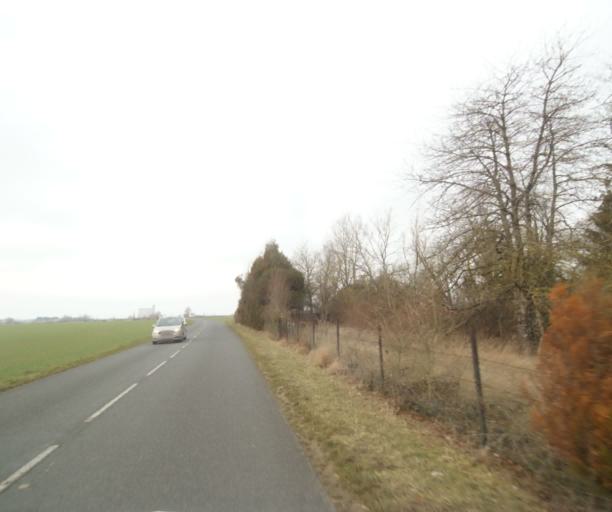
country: FR
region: Champagne-Ardenne
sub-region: Departement de la Haute-Marne
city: Villiers-en-Lieu
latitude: 48.6541
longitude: 4.7845
